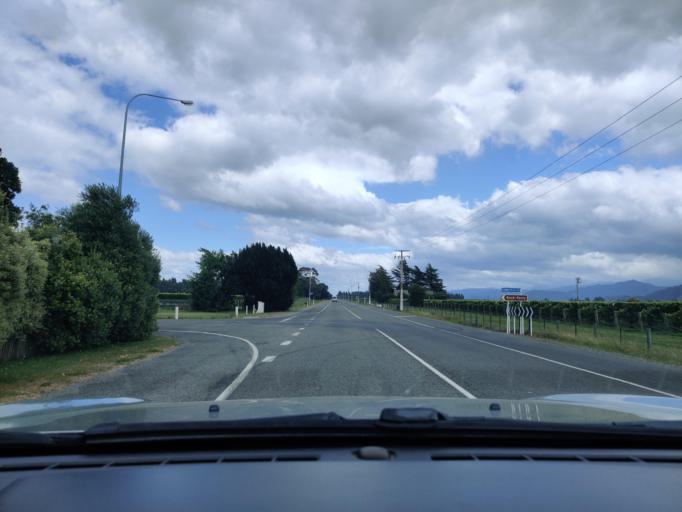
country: NZ
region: Marlborough
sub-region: Marlborough District
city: Blenheim
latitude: -41.4717
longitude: 173.9021
